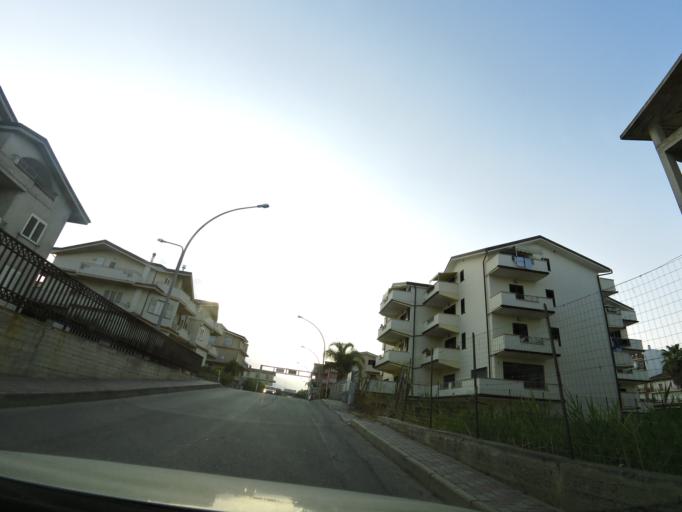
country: IT
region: Calabria
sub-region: Provincia di Reggio Calabria
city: Monasterace Marina
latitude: 38.4328
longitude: 16.5720
